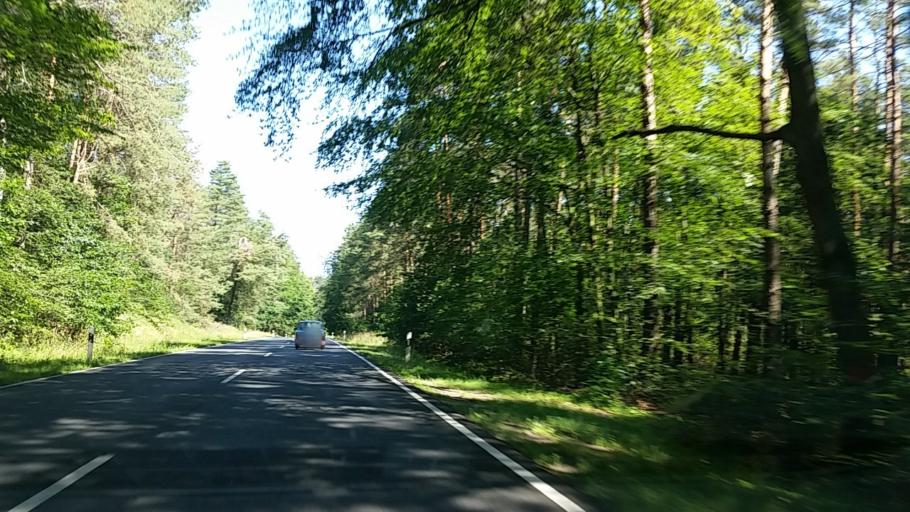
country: DE
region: Saxony-Anhalt
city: Kemberg
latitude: 51.6867
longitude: 12.6127
